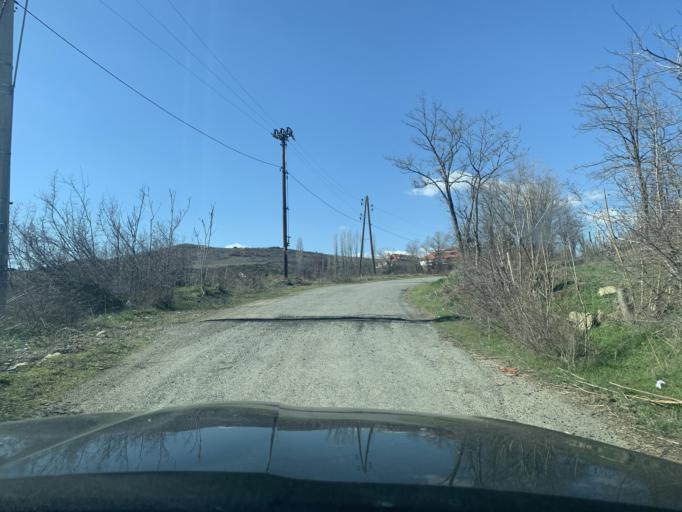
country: MK
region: Demir Kapija
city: Demir Kapija
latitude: 41.4097
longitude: 22.2297
